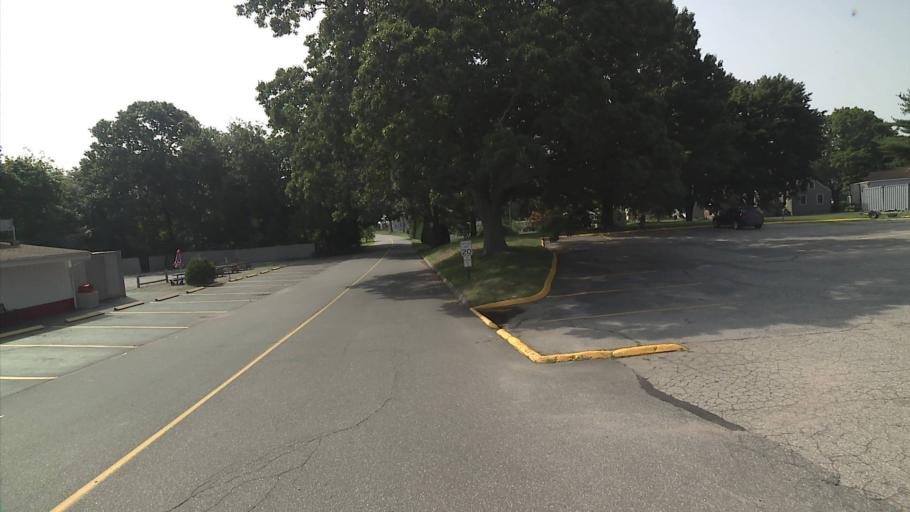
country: US
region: Connecticut
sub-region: Middlesex County
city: Westbrook Center
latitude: 41.2744
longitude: -72.4838
